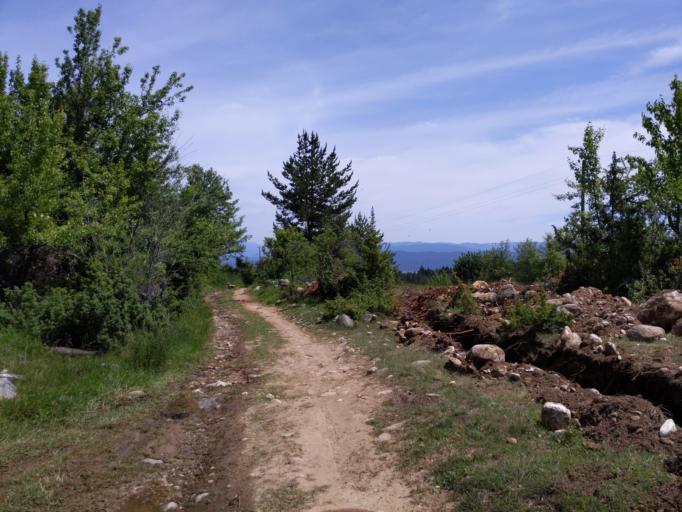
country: BG
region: Blagoevgrad
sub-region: Obshtina Bansko
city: Bansko
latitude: 41.8175
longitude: 23.4680
